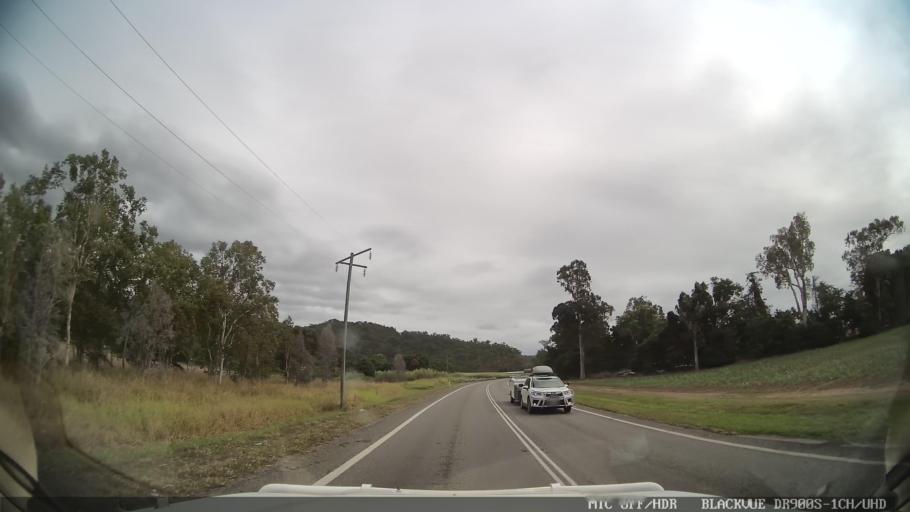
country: AU
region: Queensland
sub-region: Hinchinbrook
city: Ingham
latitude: -18.8626
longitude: 146.1707
